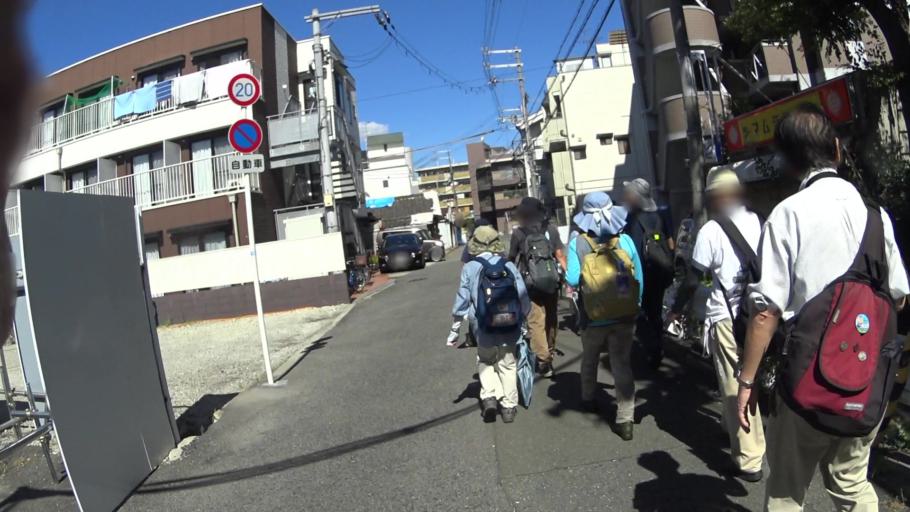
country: JP
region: Osaka
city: Yao
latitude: 34.6325
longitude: 135.5550
